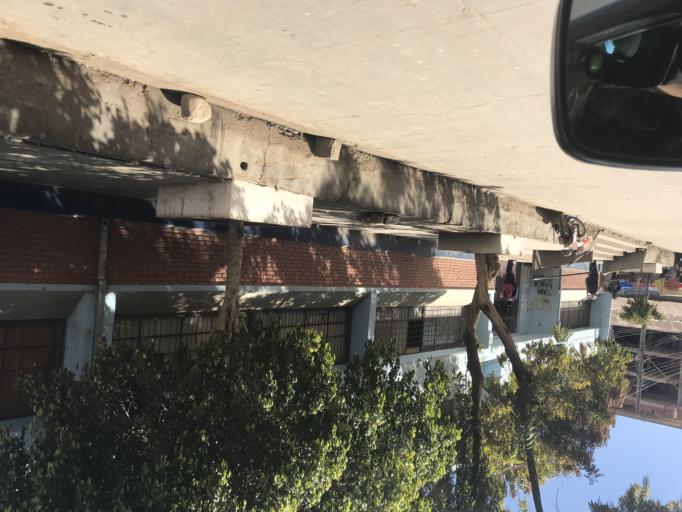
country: BO
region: Cochabamba
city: Cliza
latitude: -17.5913
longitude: -65.9338
